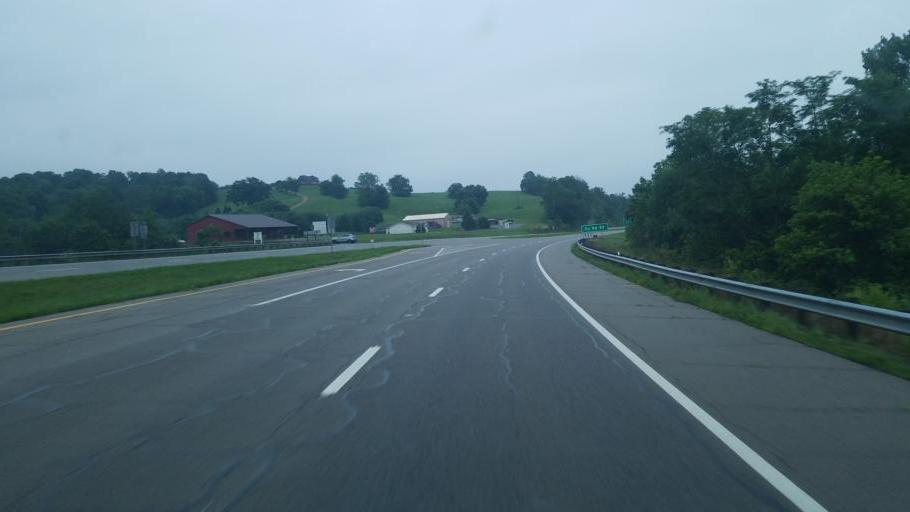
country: US
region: Ohio
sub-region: Coshocton County
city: West Lafayette
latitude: 40.2893
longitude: -81.7161
